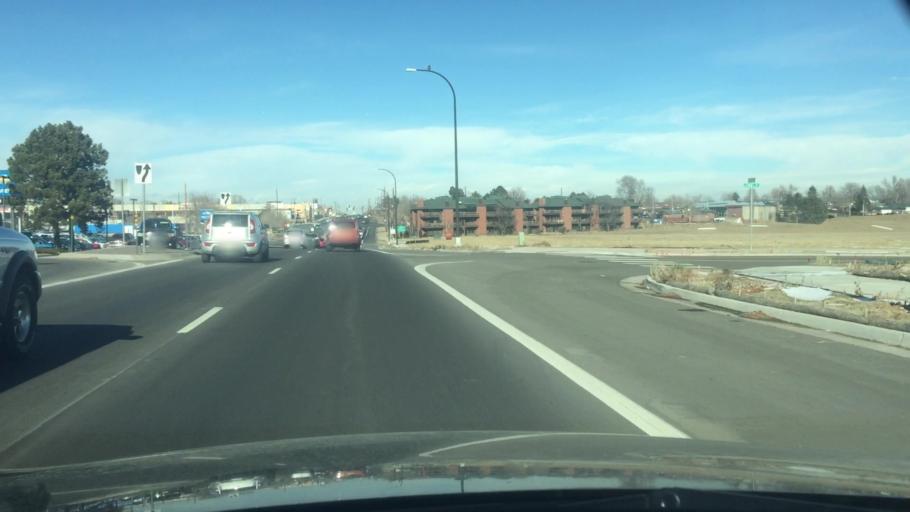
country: US
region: Colorado
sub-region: Jefferson County
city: Lakewood
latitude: 39.6787
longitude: -105.0814
